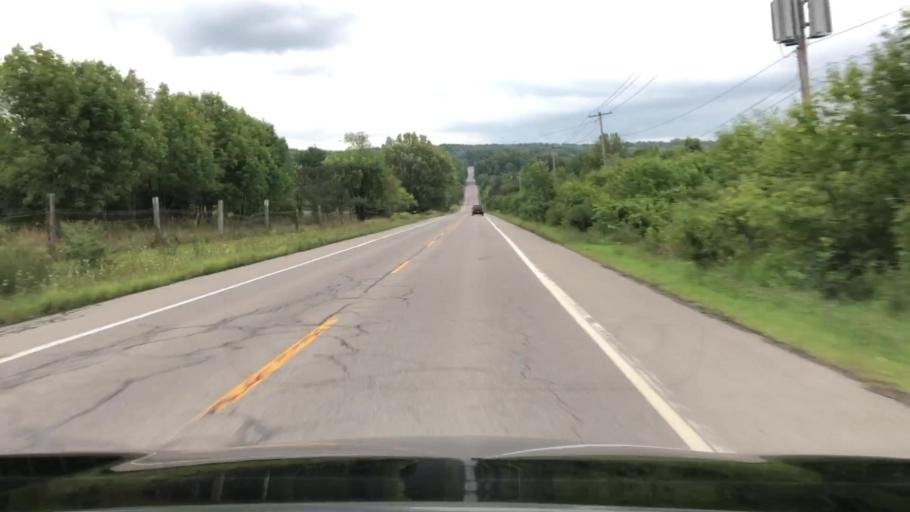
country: US
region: New York
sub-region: Erie County
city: Orchard Park
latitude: 42.7661
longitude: -78.6970
